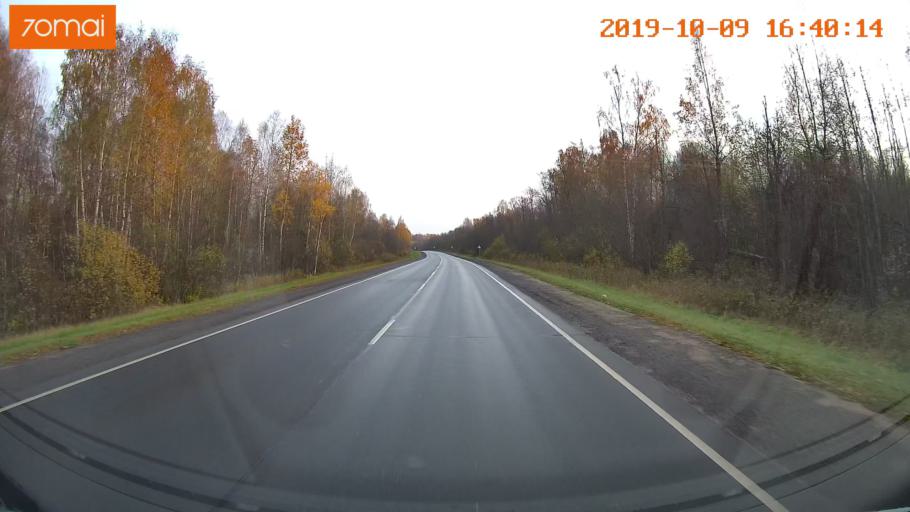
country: RU
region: Kostroma
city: Volgorechensk
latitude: 57.4865
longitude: 41.0581
